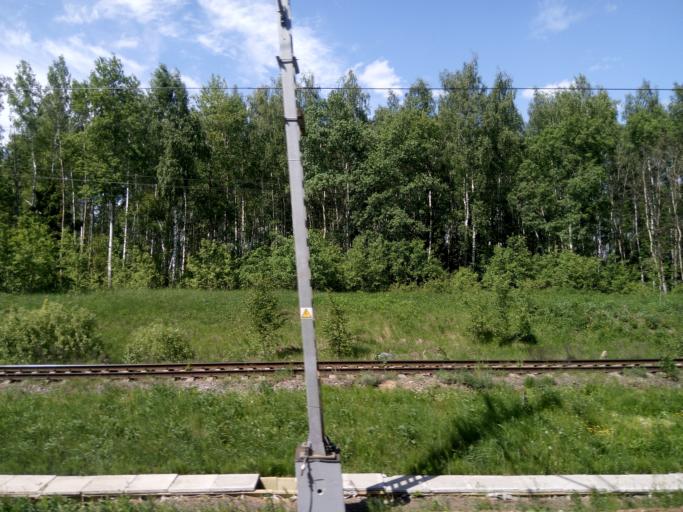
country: RU
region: Moskovskaya
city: Vostryakovo
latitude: 55.4354
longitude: 37.8556
